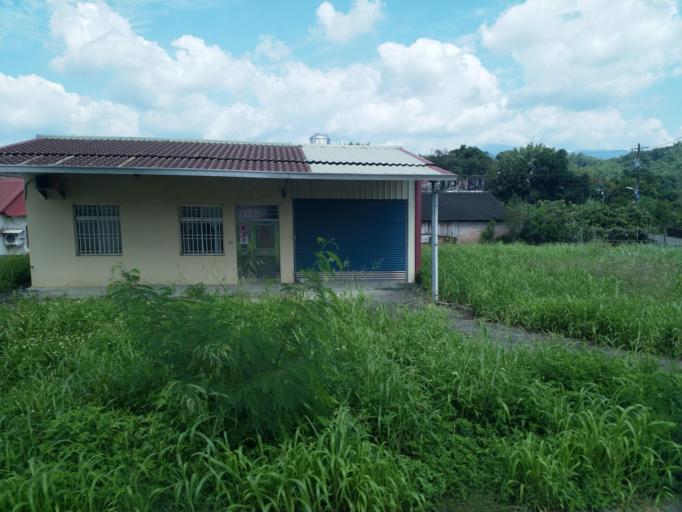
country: TW
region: Taiwan
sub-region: Pingtung
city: Pingtung
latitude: 22.8850
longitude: 120.5549
